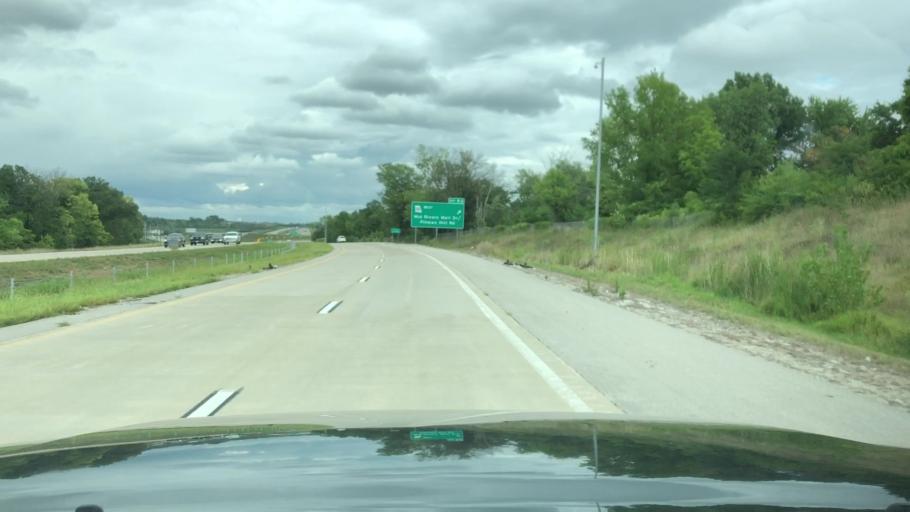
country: US
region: Missouri
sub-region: Saint Charles County
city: Cottleville
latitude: 38.7342
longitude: -90.6449
